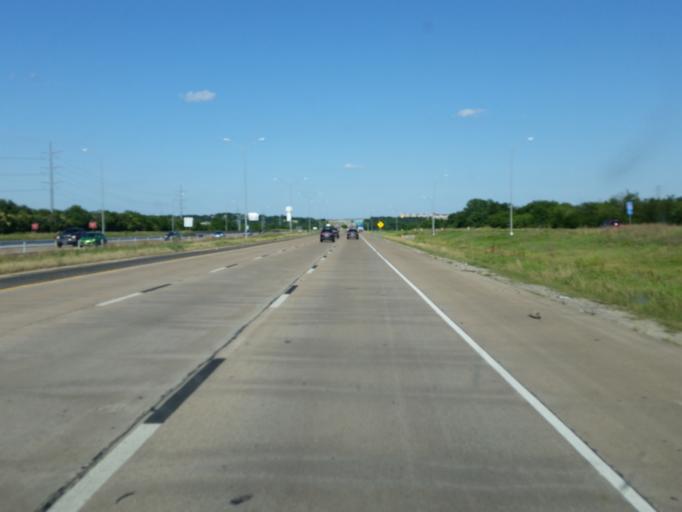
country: US
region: Texas
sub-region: Tarrant County
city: Benbrook
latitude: 32.6838
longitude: -97.4406
